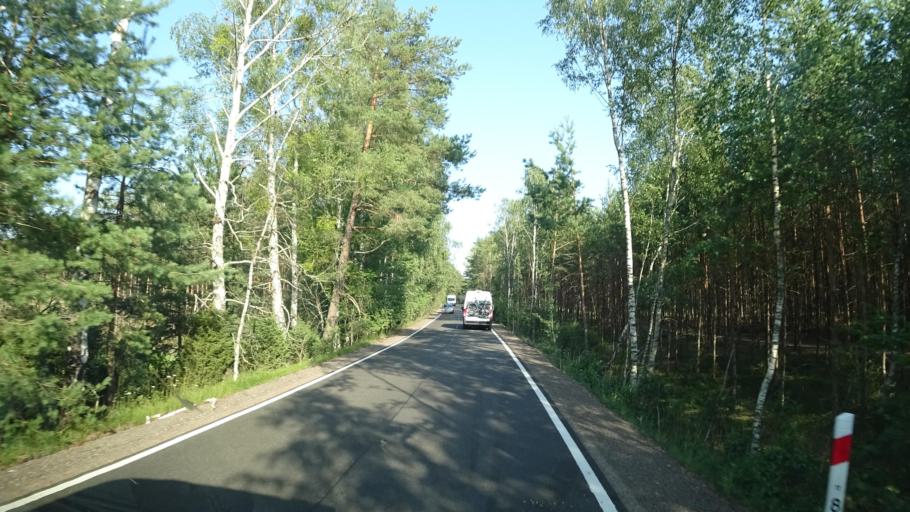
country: PL
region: Pomeranian Voivodeship
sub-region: Powiat chojnicki
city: Chojnice
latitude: 53.8552
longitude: 17.5561
